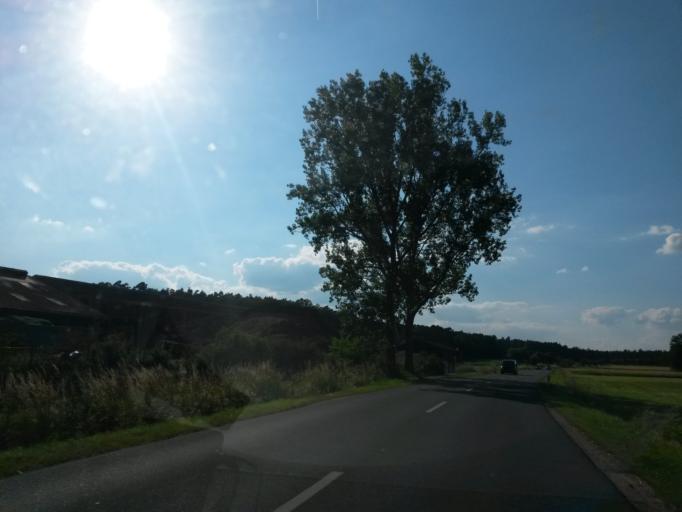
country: DE
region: Bavaria
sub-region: Regierungsbezirk Mittelfranken
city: Zirndorf
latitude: 49.4496
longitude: 10.9243
